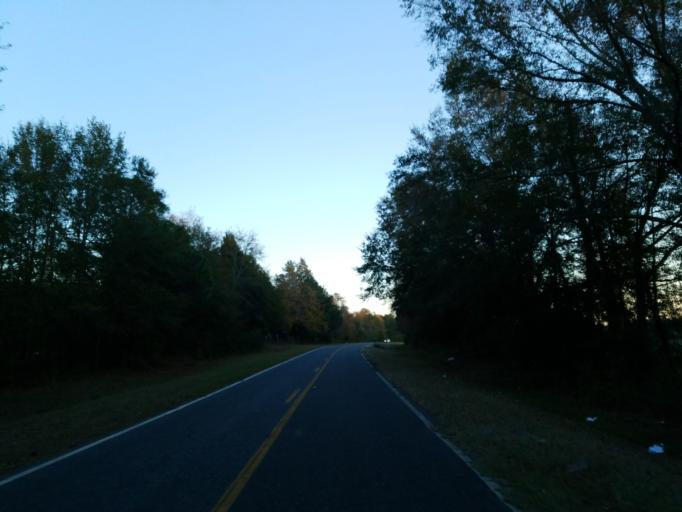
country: US
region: Georgia
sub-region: Ben Hill County
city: Fitzgerald
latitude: 31.6632
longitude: -83.3926
